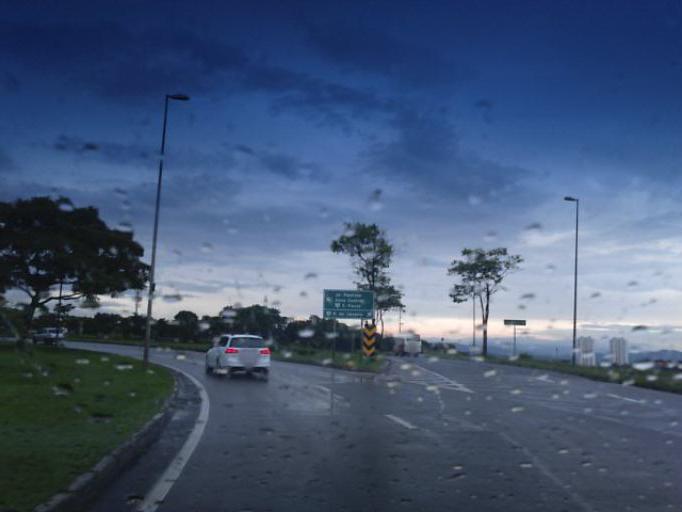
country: BR
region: Sao Paulo
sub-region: Sao Jose Dos Campos
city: Sao Jose dos Campos
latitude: -23.1949
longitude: -45.8660
